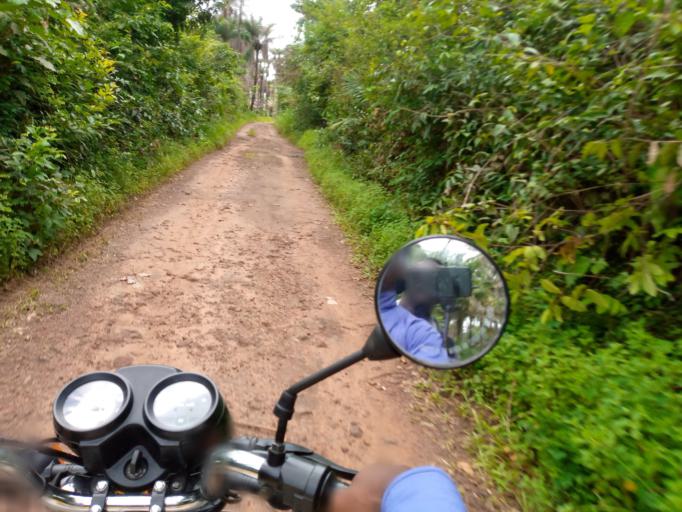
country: SL
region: Northern Province
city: Mange
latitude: 8.9836
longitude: -12.8195
